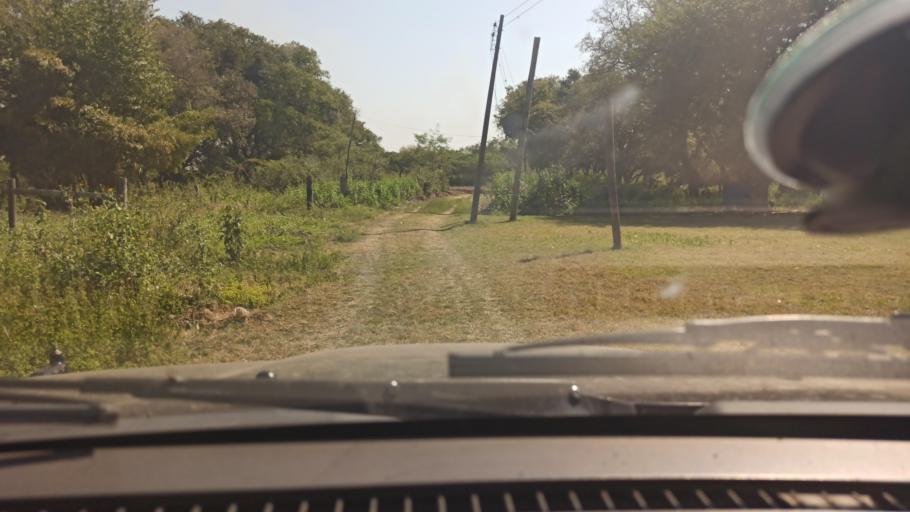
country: PY
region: Asuncion
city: Asuncion
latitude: -25.3520
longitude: -57.6698
